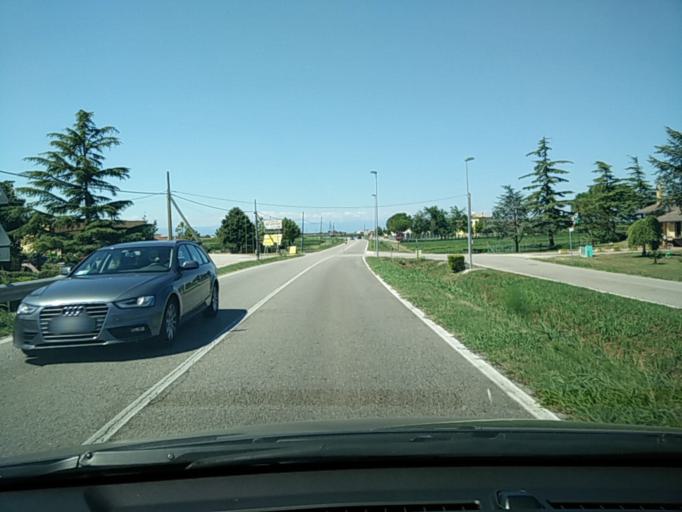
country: IT
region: Veneto
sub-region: Provincia di Venezia
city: Caorle
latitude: 45.6298
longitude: 12.8606
